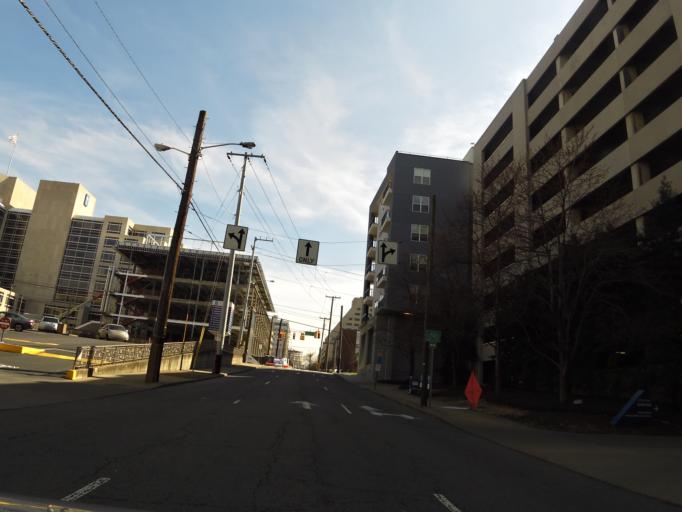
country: US
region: Tennessee
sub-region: Davidson County
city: Nashville
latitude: 36.1532
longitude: -86.8032
